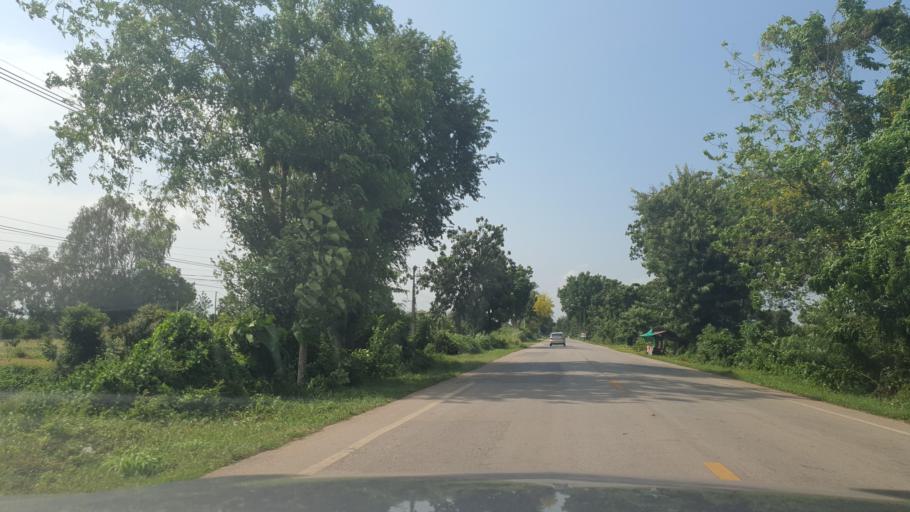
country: TH
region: Sukhothai
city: Si Samrong
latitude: 17.1830
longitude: 99.8518
